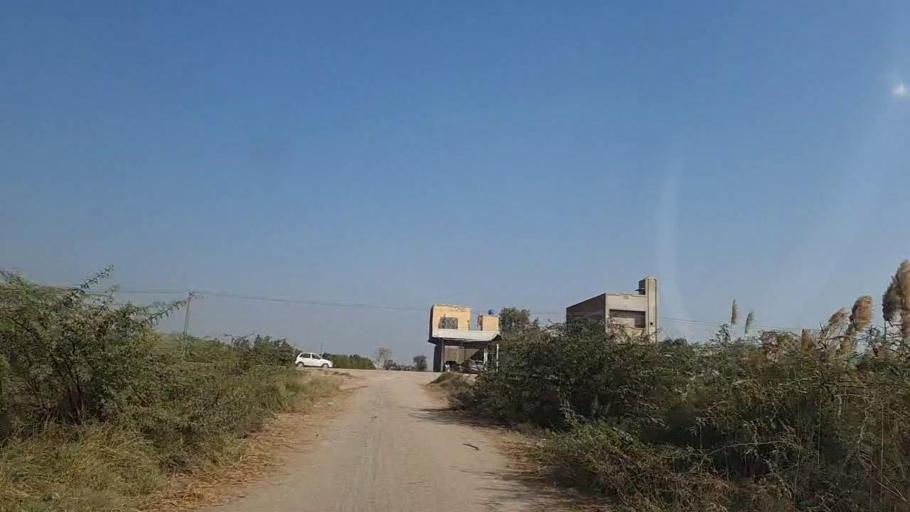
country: PK
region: Sindh
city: Daur
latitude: 26.4583
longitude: 68.3055
